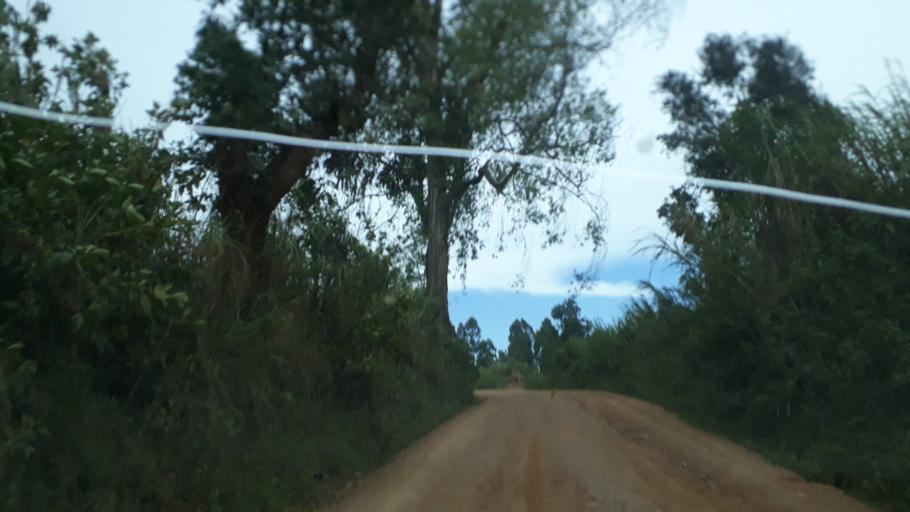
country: CD
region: Eastern Province
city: Bunia
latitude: 1.9276
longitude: 30.5135
